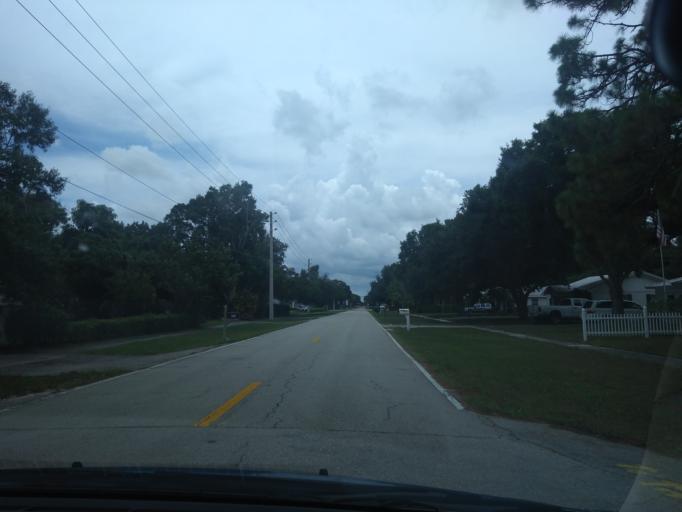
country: US
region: Florida
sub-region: Indian River County
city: Vero Beach
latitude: 27.6402
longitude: -80.4205
